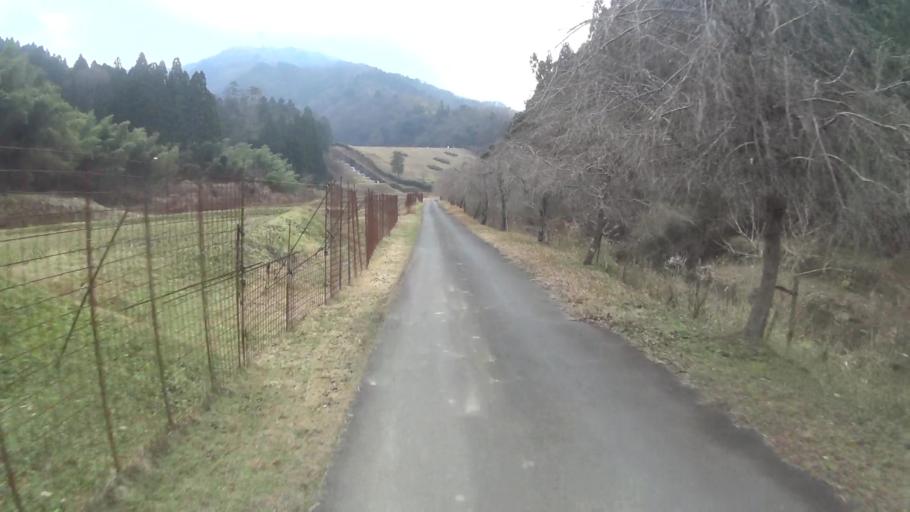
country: JP
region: Kyoto
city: Maizuru
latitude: 35.4448
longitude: 135.4398
